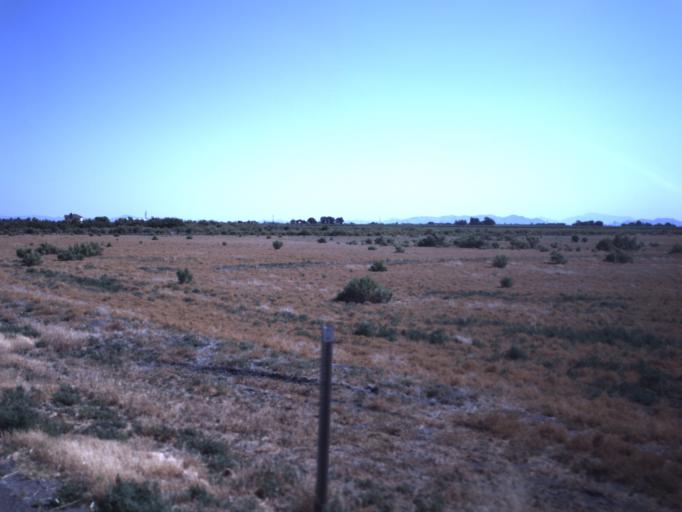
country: US
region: Utah
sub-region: Millard County
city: Delta
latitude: 39.3036
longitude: -112.6525
